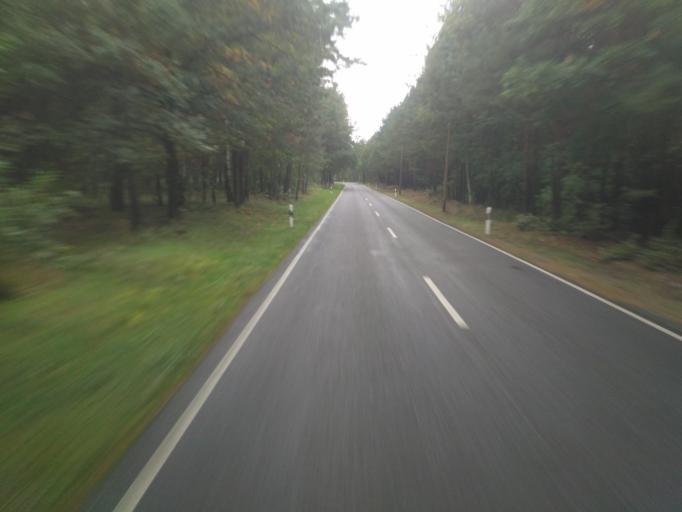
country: DE
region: Saxony
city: Konigswartha
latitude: 51.3029
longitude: 14.2995
